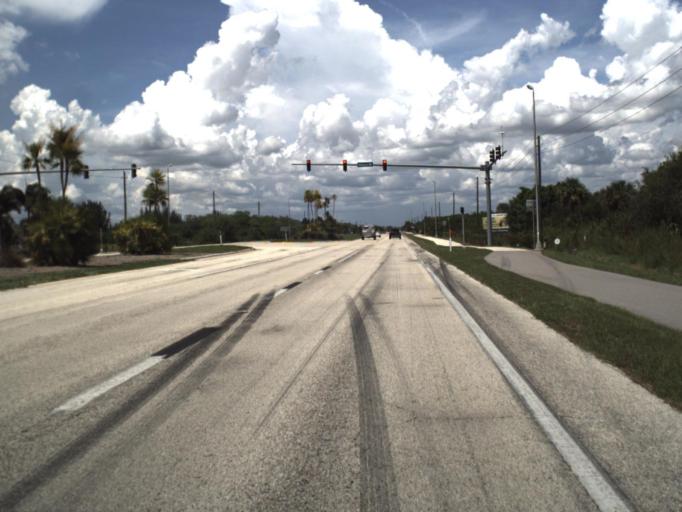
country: US
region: Florida
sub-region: Charlotte County
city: Charlotte Park
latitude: 26.8982
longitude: -82.0301
